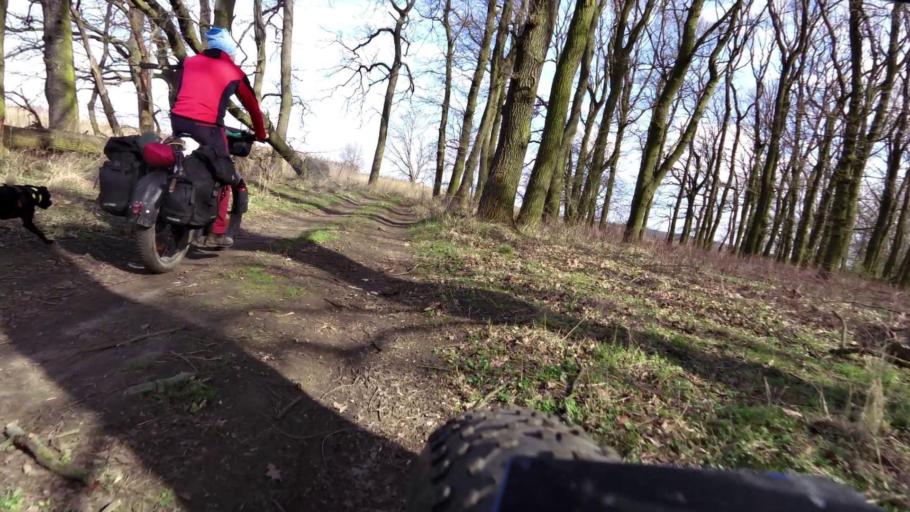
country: PL
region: Lubusz
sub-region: Powiat slubicki
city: Slubice
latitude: 52.3333
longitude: 14.5647
